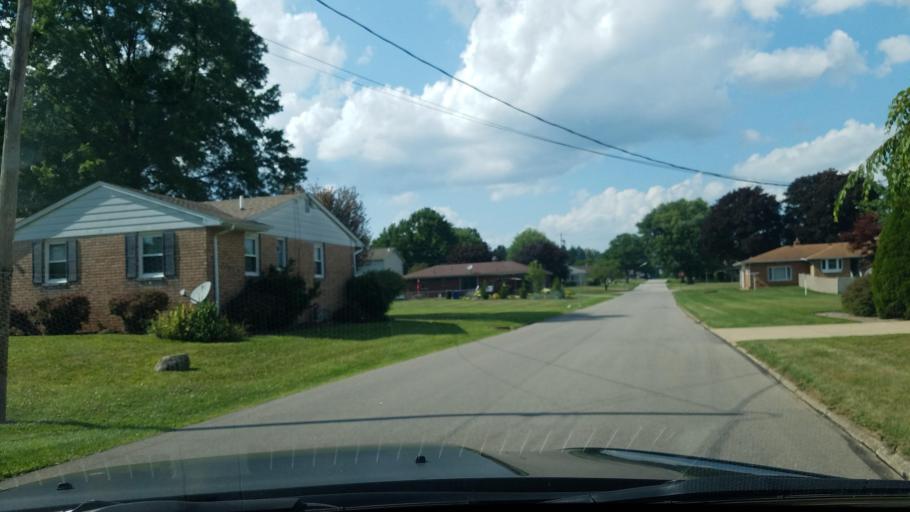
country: US
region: Ohio
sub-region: Mahoning County
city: Struthers
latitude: 41.0393
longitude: -80.6113
